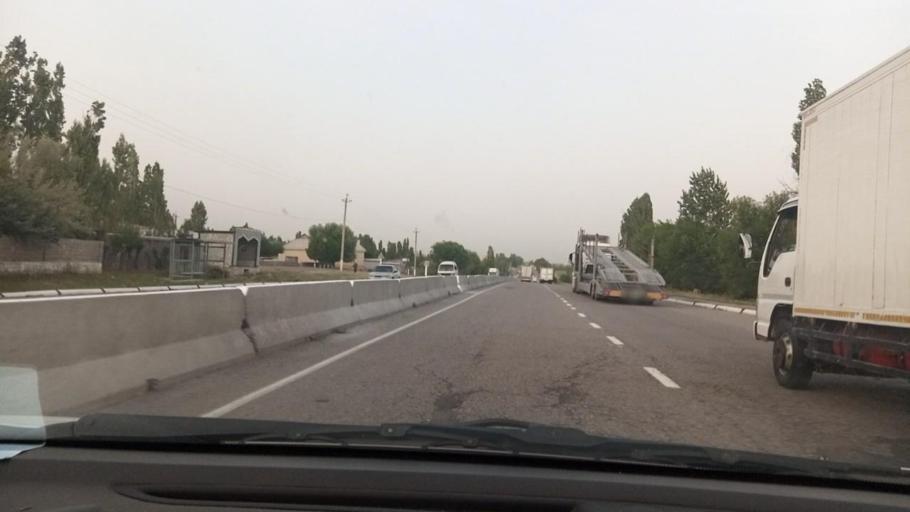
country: UZ
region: Toshkent
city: Angren
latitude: 40.9679
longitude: 69.9749
